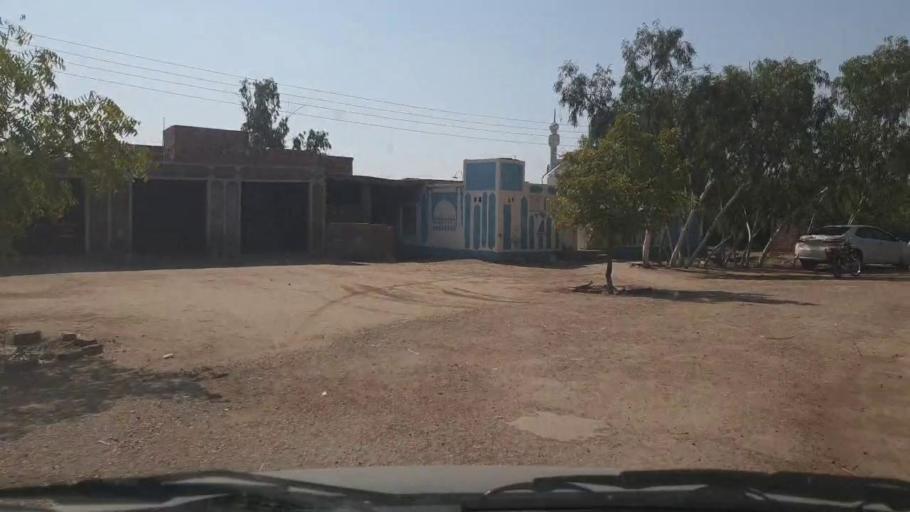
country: PK
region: Sindh
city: Samaro
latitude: 25.2373
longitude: 69.3244
